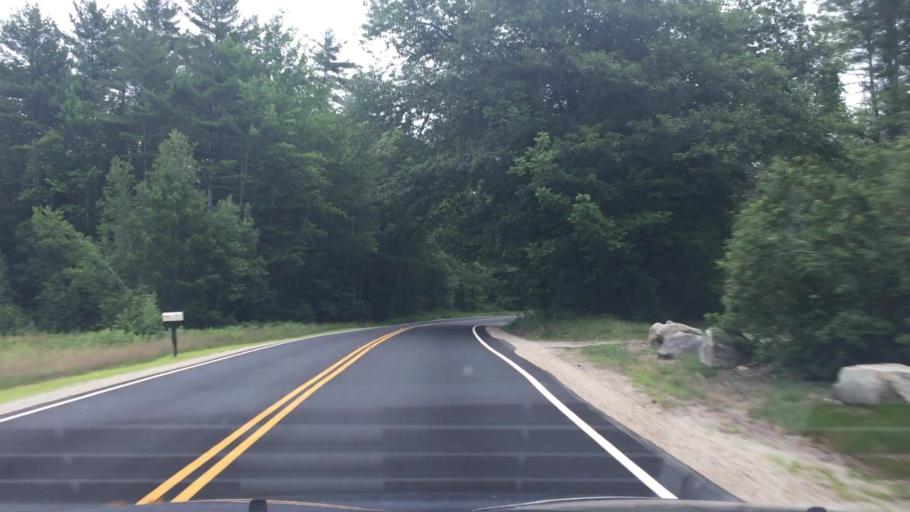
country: US
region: New Hampshire
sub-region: Carroll County
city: Freedom
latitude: 43.8431
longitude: -71.0838
